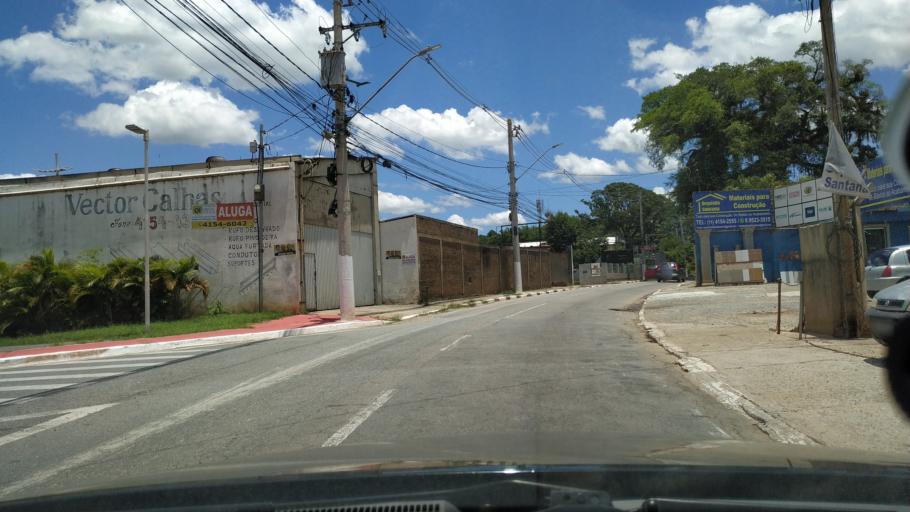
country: BR
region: Sao Paulo
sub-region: Santana De Parnaiba
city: Santana de Parnaiba
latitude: -23.4402
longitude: -46.9113
